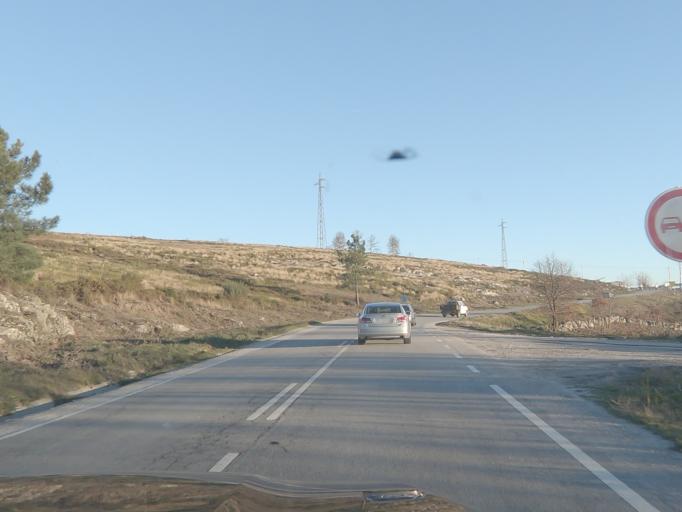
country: PT
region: Vila Real
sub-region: Ribeira de Pena
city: Ribeira de Pena
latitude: 41.4991
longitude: -7.7322
